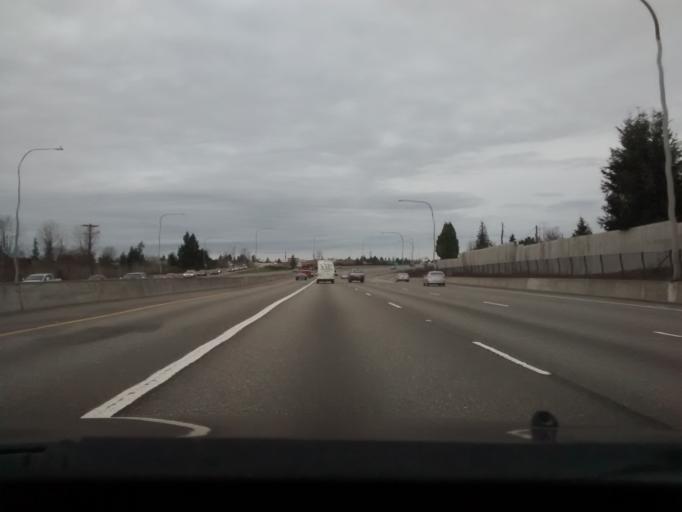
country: US
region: Washington
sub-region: Pierce County
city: Fircrest
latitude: 47.2505
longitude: -122.5114
